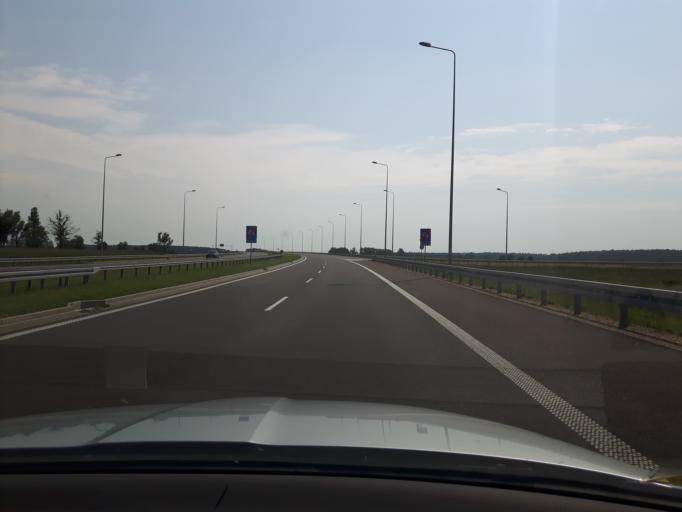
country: PL
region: Masovian Voivodeship
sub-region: Powiat mlawski
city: Wieczfnia Koscielna
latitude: 53.2269
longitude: 20.4191
